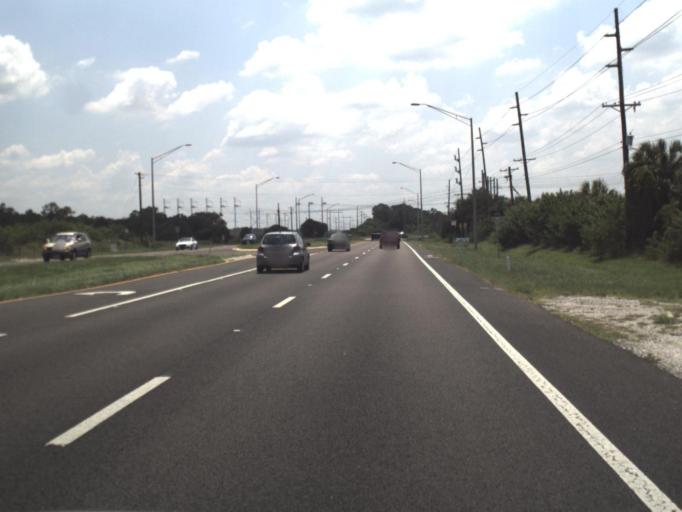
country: US
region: Florida
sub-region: Hillsborough County
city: Apollo Beach
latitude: 27.7854
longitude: -82.3846
